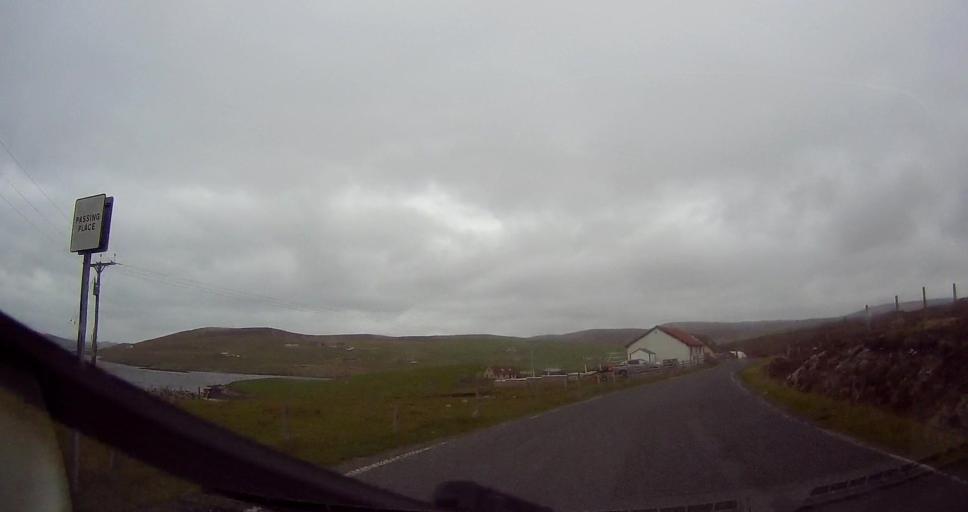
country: GB
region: Scotland
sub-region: Shetland Islands
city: Lerwick
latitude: 60.2969
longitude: -1.3634
